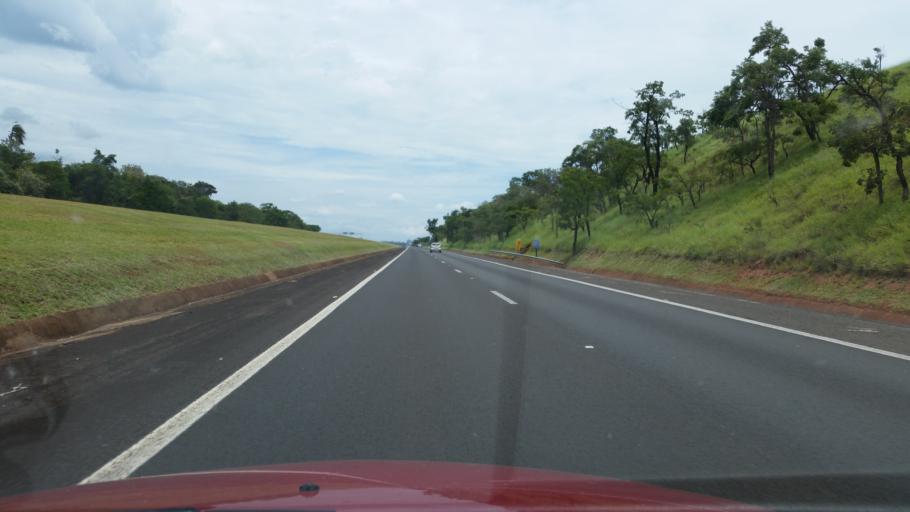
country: BR
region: Sao Paulo
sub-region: Avare
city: Avare
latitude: -22.9741
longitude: -48.7894
